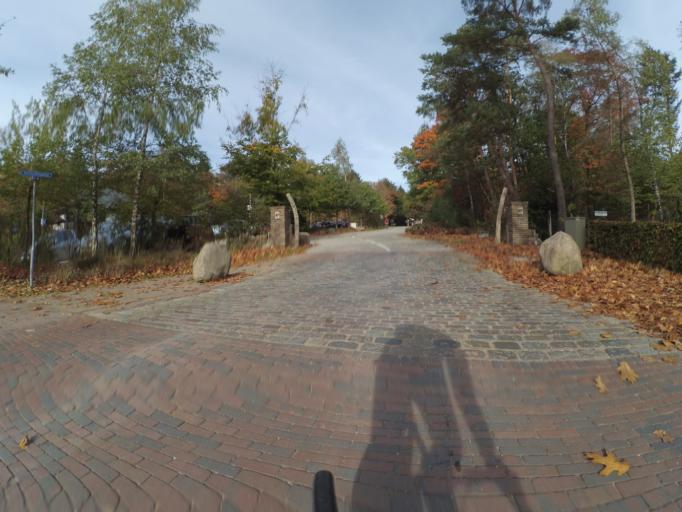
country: NL
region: Overijssel
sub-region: Gemeente Hof van Twente
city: Markelo
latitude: 52.2977
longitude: 6.4204
